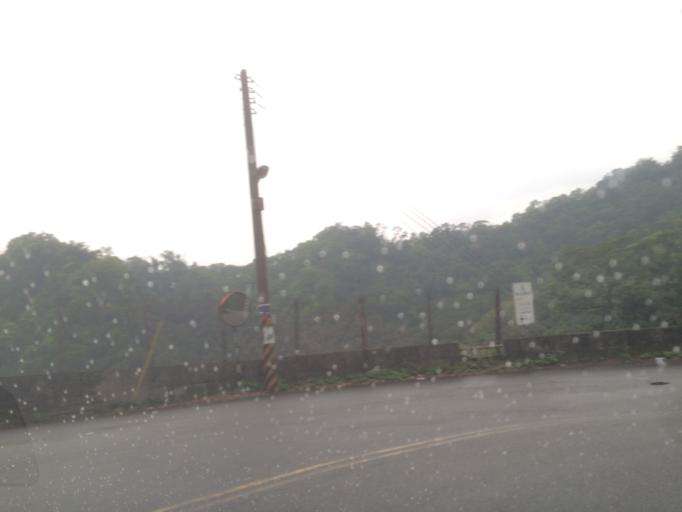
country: TW
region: Taiwan
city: Fengyuan
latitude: 24.1698
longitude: 120.8235
